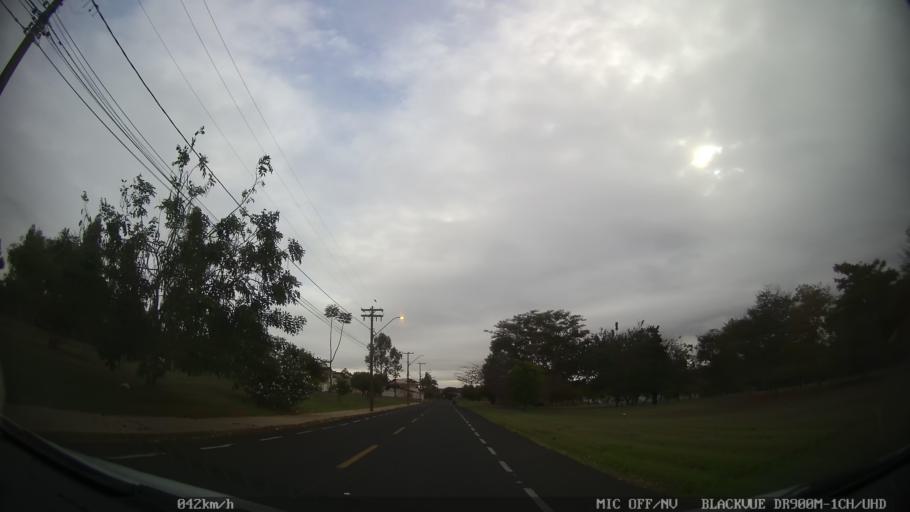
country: BR
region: Sao Paulo
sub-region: Sao Jose Do Rio Preto
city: Sao Jose do Rio Preto
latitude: -20.8374
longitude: -49.3952
